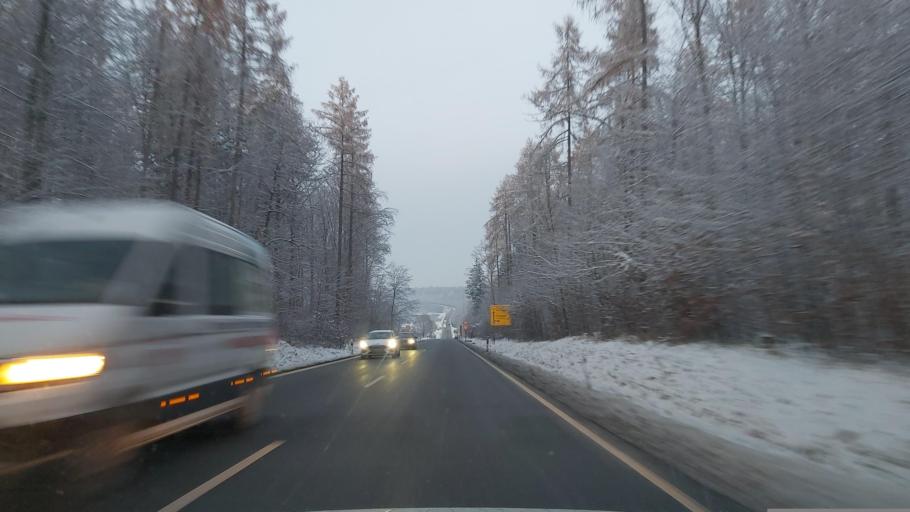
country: DE
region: Baden-Wuerttemberg
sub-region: Regierungsbezirk Stuttgart
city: Grossbettlingen
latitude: 48.5726
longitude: 9.3182
